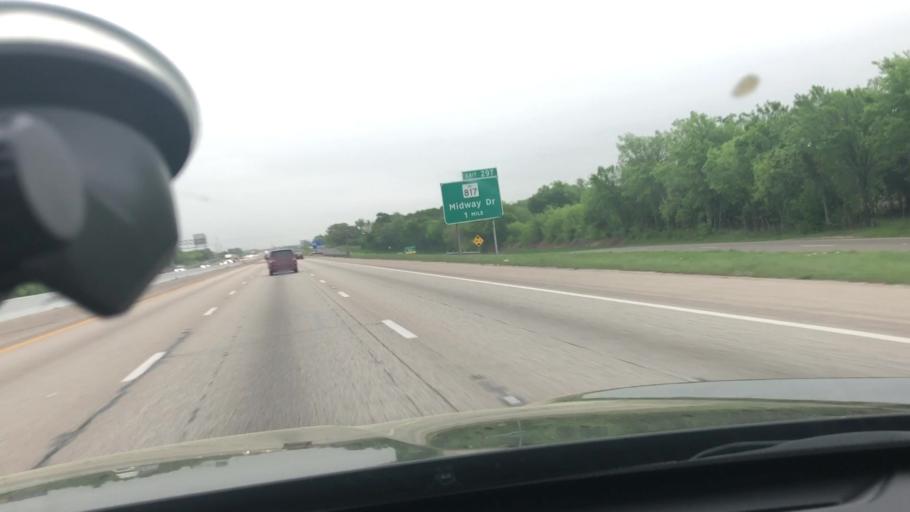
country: US
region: Texas
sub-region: Bell County
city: Belton
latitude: 31.0659
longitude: -97.4293
